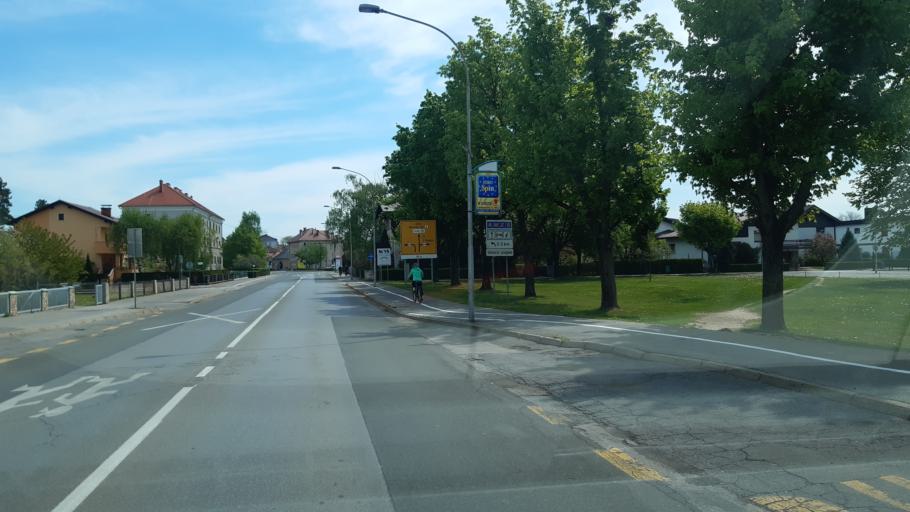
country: SI
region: Murska Sobota
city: Murska Sobota
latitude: 46.6614
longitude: 16.1520
